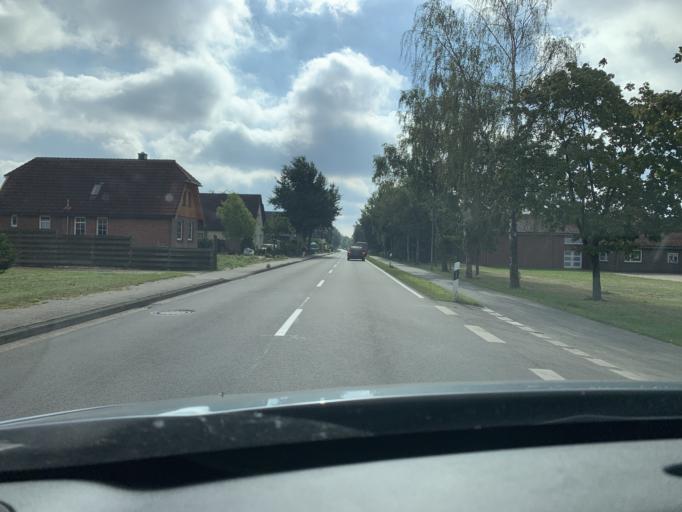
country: DE
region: Lower Saxony
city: Edewecht
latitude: 53.1005
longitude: 8.0800
